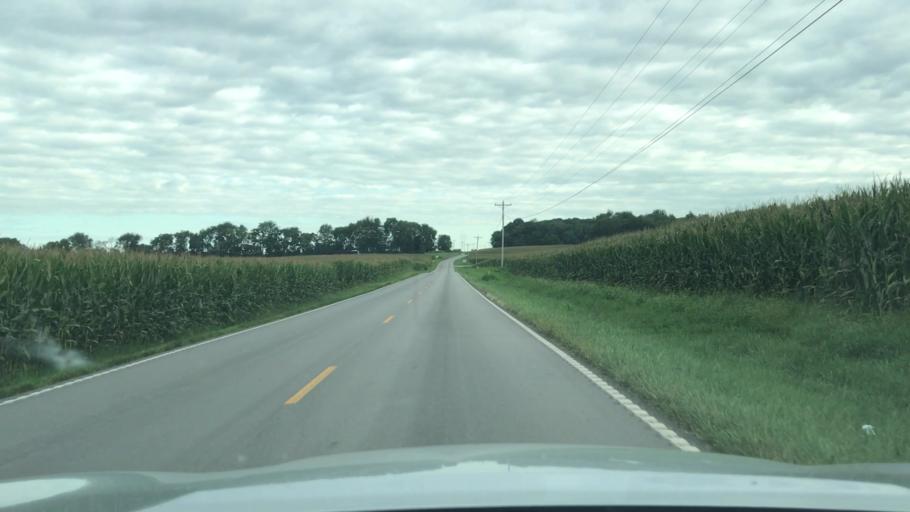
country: US
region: Kentucky
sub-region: Todd County
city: Guthrie
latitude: 36.6798
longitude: -87.1998
